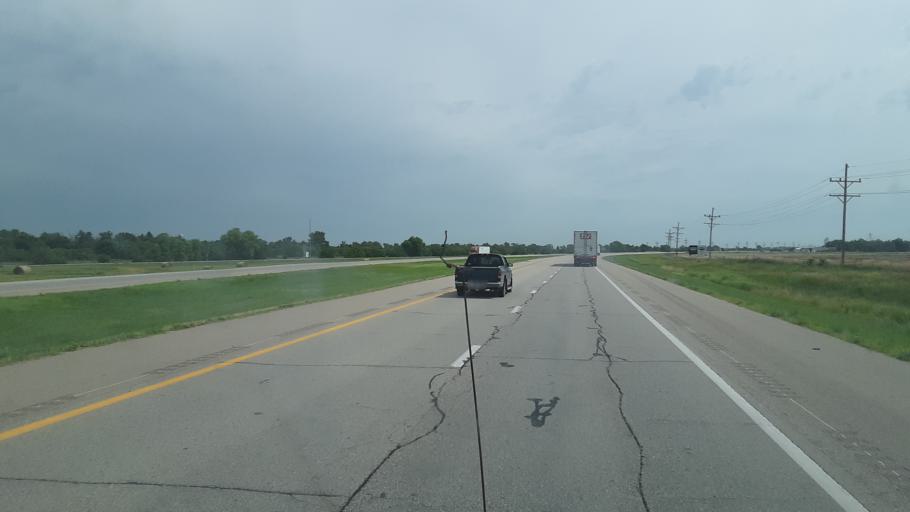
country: US
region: Kansas
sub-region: Reno County
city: South Hutchinson
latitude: 37.9892
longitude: -98.0435
